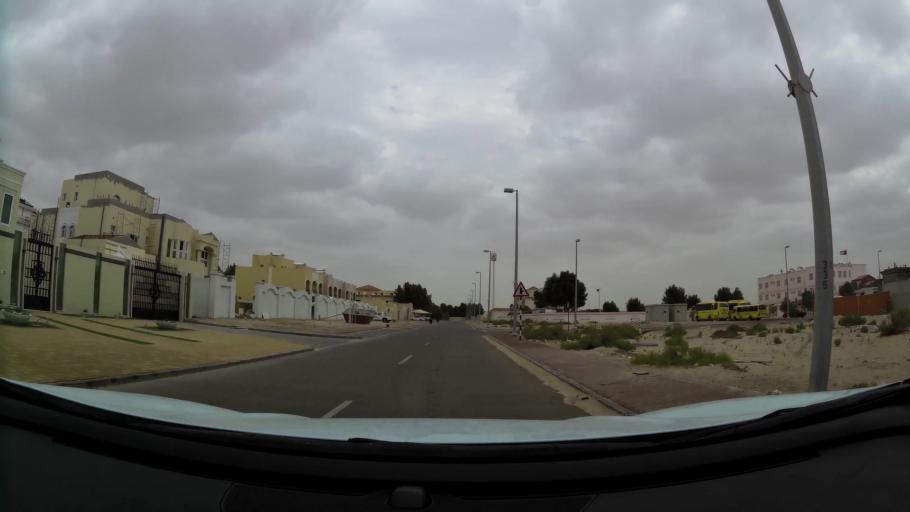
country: AE
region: Abu Dhabi
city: Abu Dhabi
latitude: 24.3768
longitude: 54.6391
